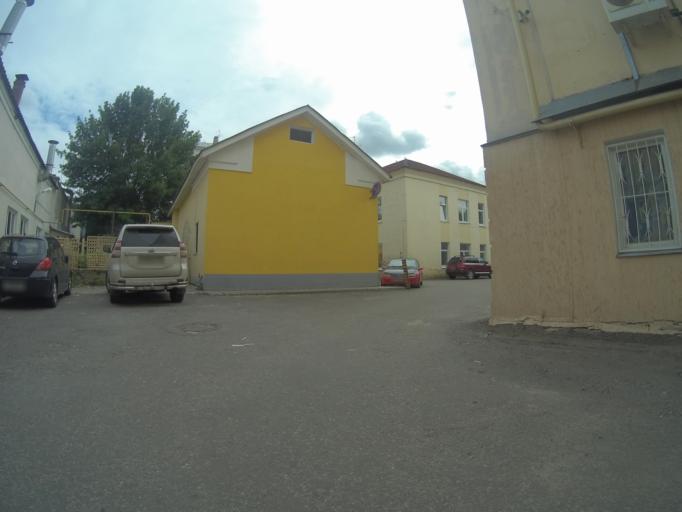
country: RU
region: Vladimir
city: Vladimir
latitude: 56.1283
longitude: 40.3949
